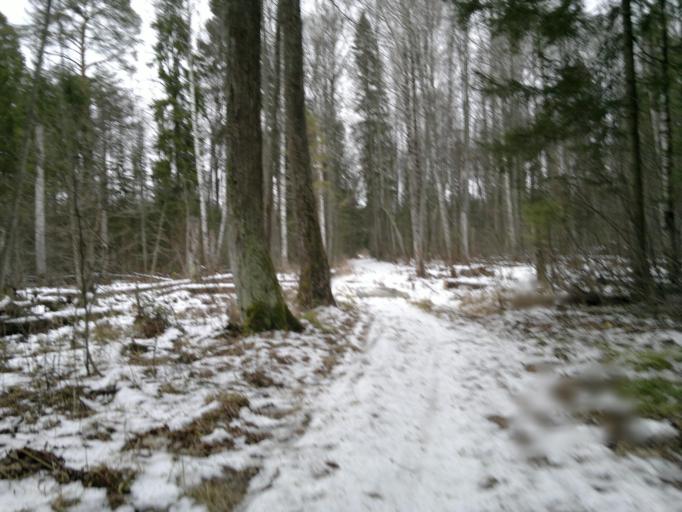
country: RU
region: Mariy-El
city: Yoshkar-Ola
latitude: 56.6083
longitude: 47.9584
